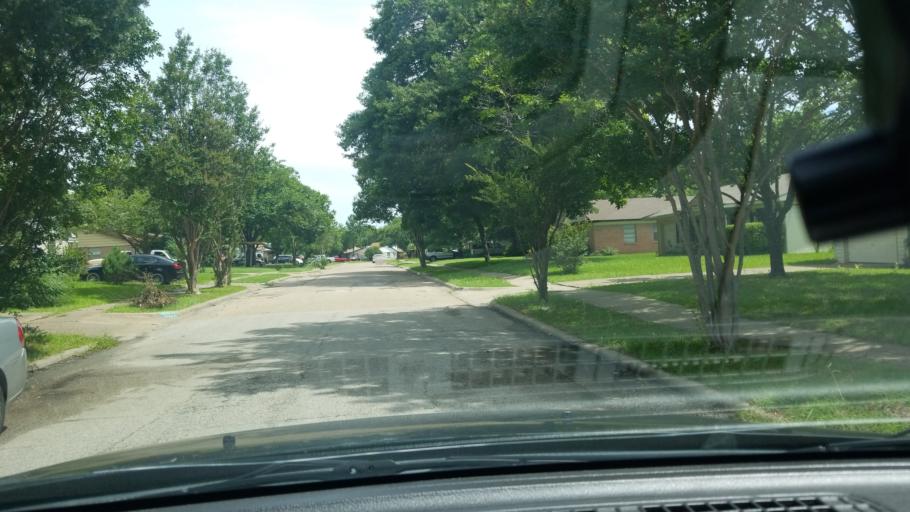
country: US
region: Texas
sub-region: Dallas County
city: Mesquite
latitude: 32.7544
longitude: -96.5798
